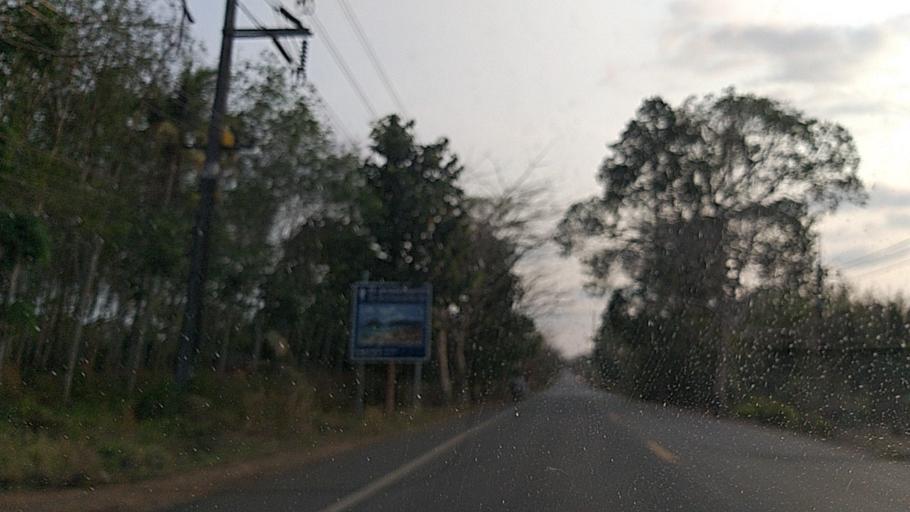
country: TH
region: Trat
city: Khao Saming
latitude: 12.3168
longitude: 102.3568
